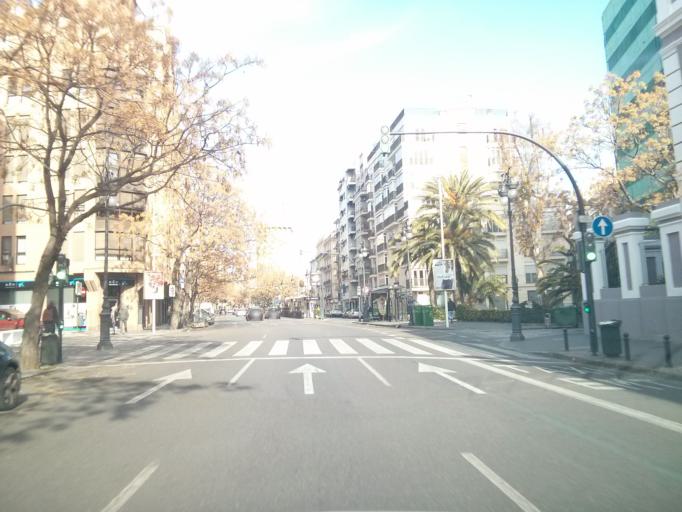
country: ES
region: Valencia
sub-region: Provincia de Valencia
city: Valencia
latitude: 39.4734
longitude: -0.3839
